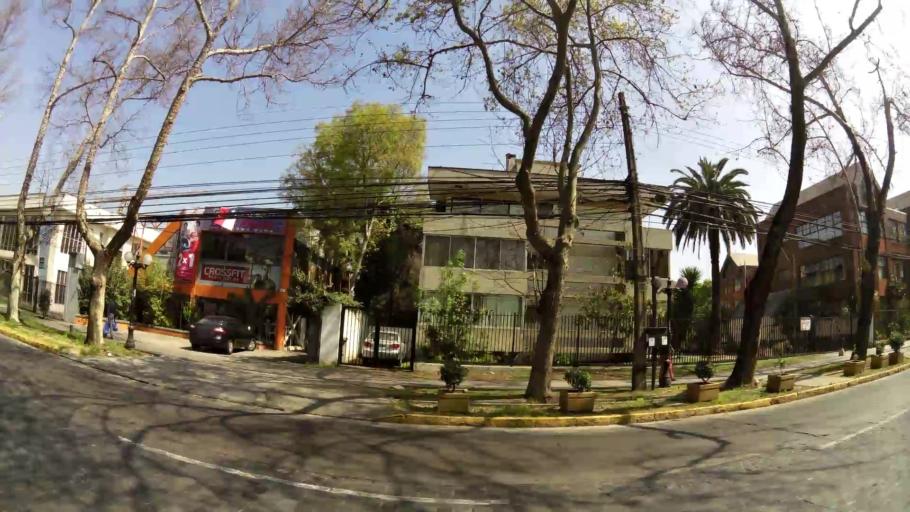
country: CL
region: Santiago Metropolitan
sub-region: Provincia de Santiago
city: Villa Presidente Frei, Nunoa, Santiago, Chile
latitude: -33.4409
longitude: -70.6070
